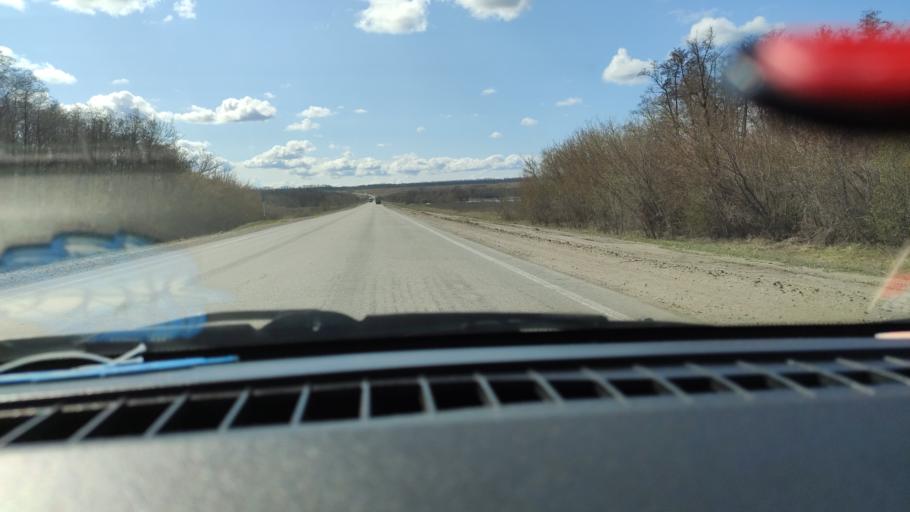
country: RU
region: Samara
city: Varlamovo
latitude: 53.1392
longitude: 48.2859
